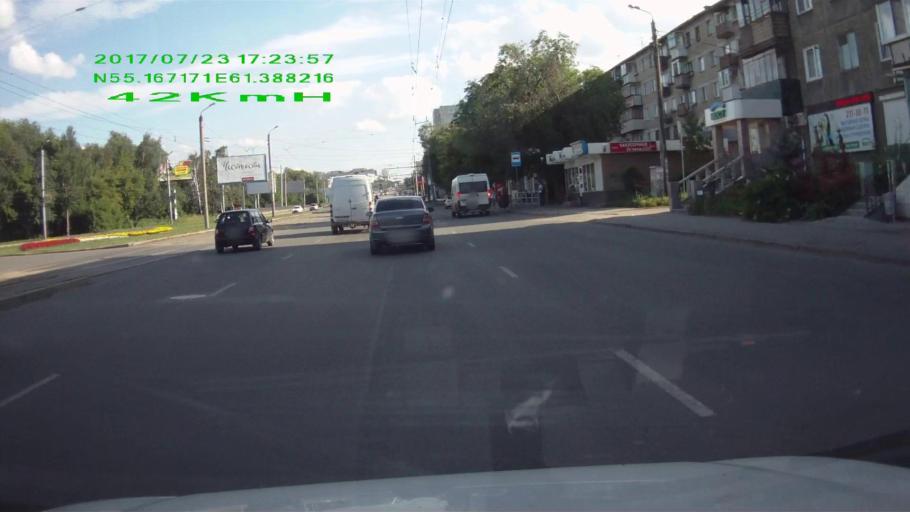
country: RU
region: Chelyabinsk
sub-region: Gorod Chelyabinsk
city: Chelyabinsk
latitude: 55.1669
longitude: 61.3882
